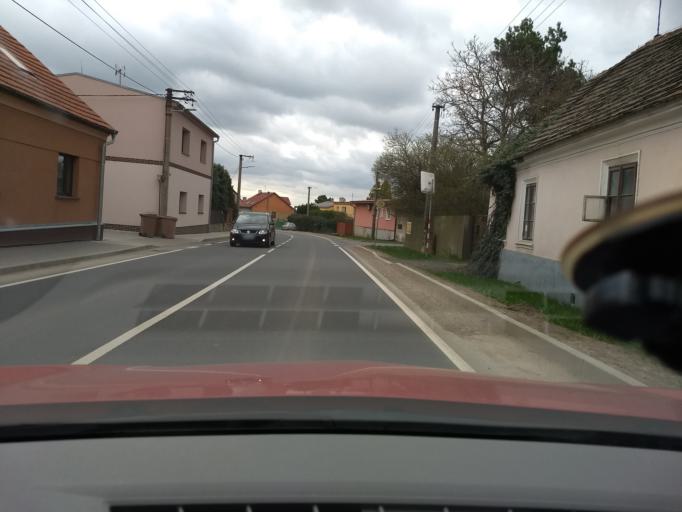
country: CZ
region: Central Bohemia
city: Unhost'
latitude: 50.0522
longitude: 14.1684
